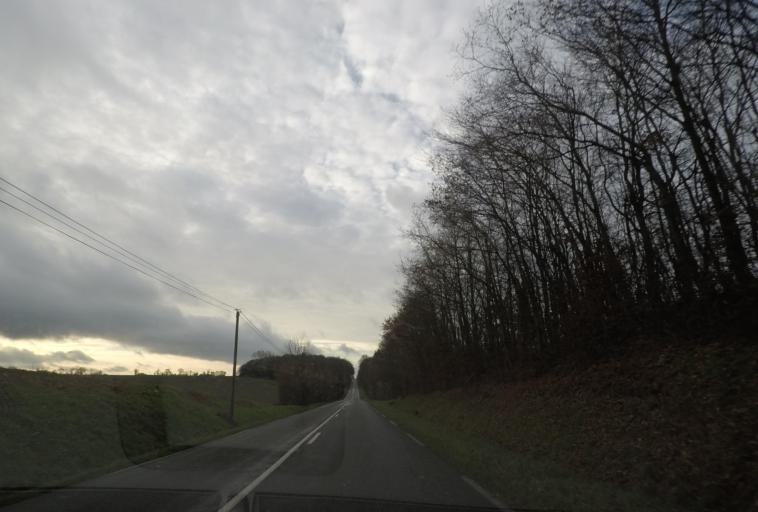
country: FR
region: Pays de la Loire
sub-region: Departement de la Sarthe
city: Saint-Calais
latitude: 47.9617
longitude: 0.7564
